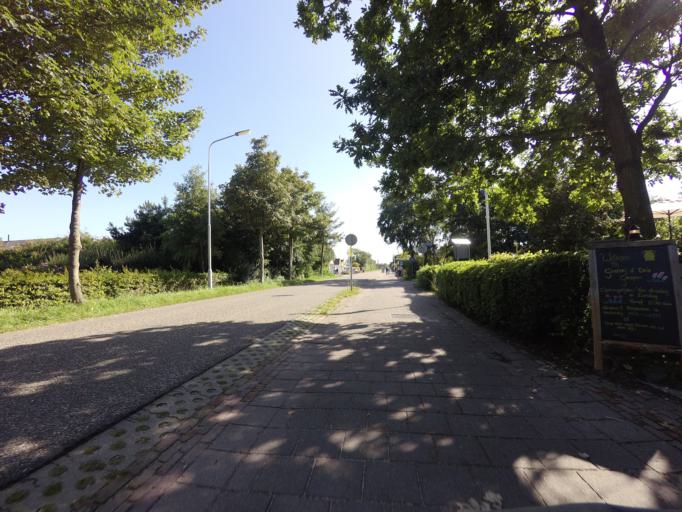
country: NL
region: Friesland
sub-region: Gemeente Terschelling
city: West-Terschelling
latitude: 53.3902
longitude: 5.2847
